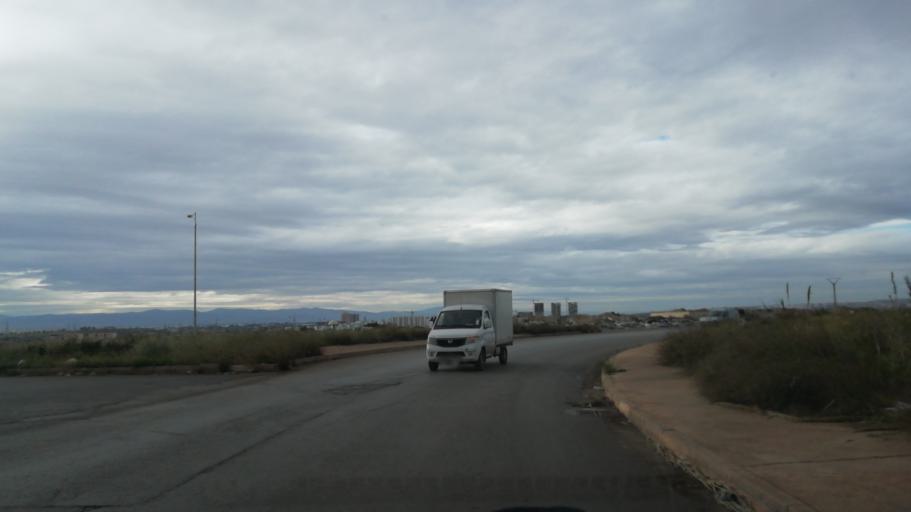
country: DZ
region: Oran
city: Oran
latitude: 35.6924
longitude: -0.5981
